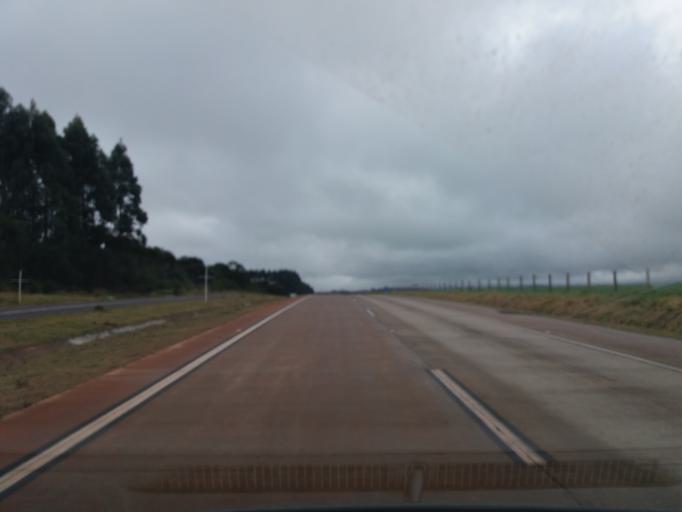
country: BR
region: Parana
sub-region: Cascavel
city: Cascavel
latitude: -25.0600
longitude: -53.5625
